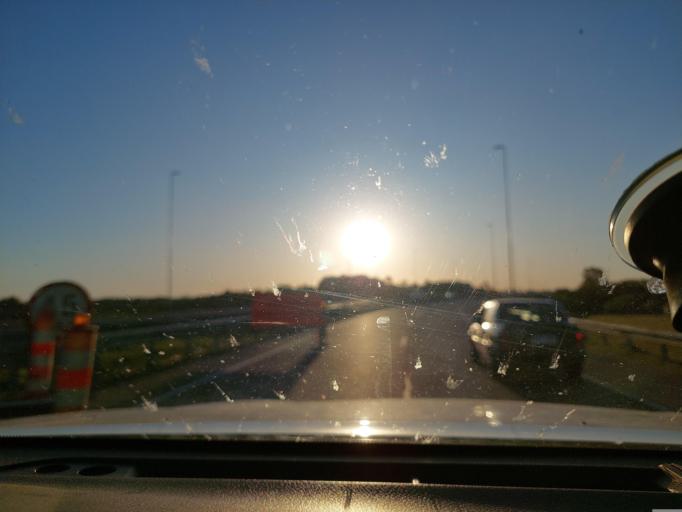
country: UY
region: Canelones
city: Pando
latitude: -34.7124
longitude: -55.9368
